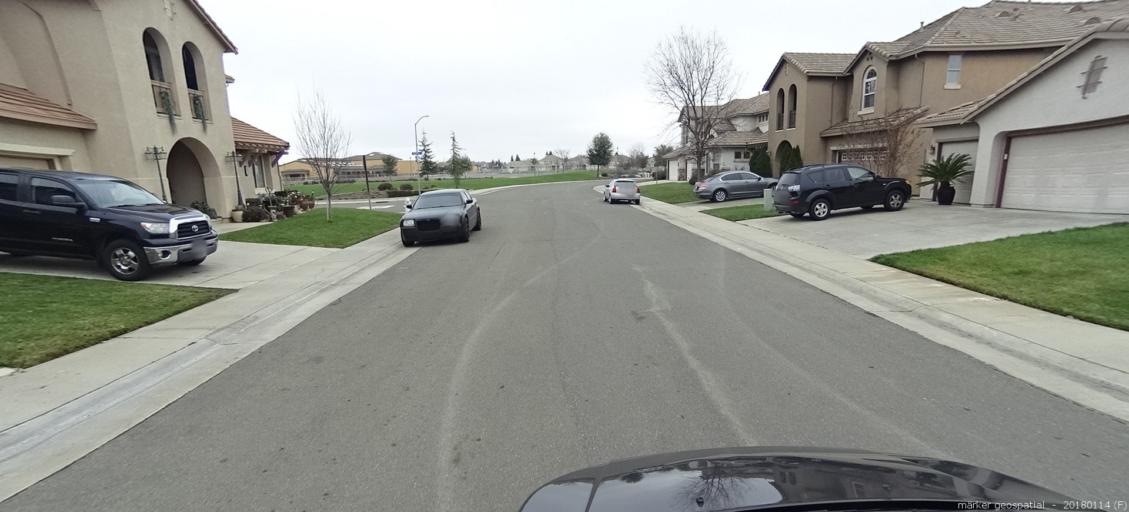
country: US
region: California
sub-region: Sacramento County
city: Rancho Cordova
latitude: 38.5439
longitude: -121.2362
